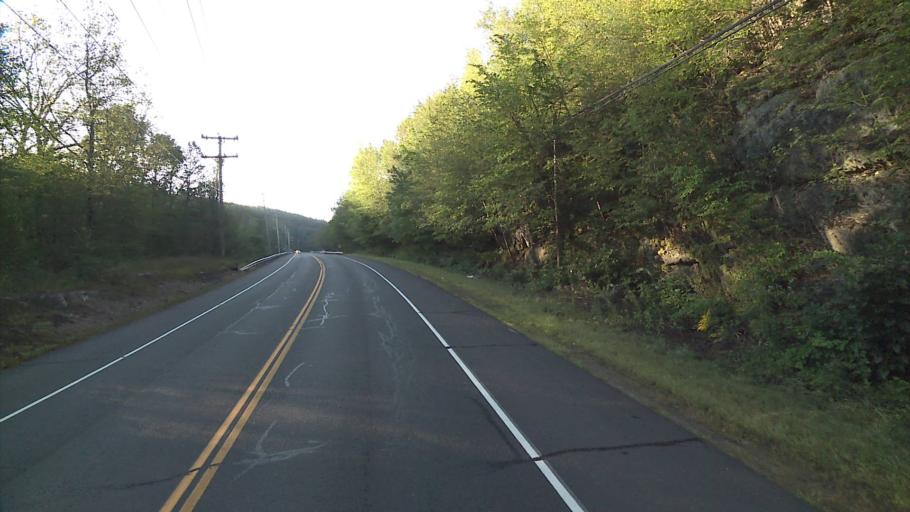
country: US
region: Connecticut
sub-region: Tolland County
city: Stafford Springs
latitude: 41.9306
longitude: -72.3090
